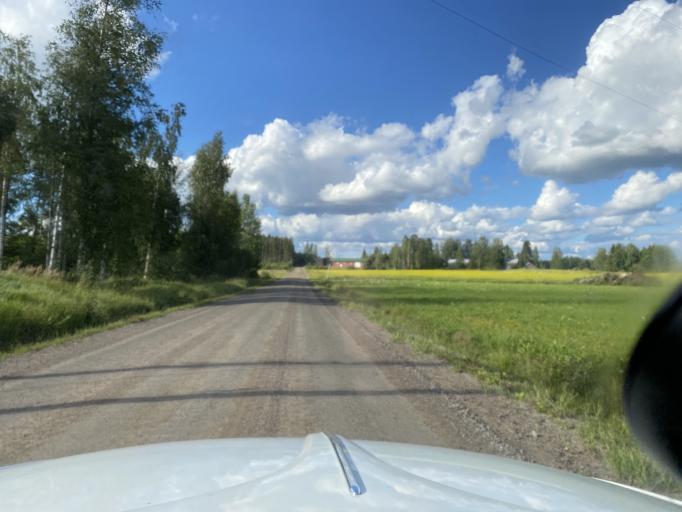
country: FI
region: Pirkanmaa
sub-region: Lounais-Pirkanmaa
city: Punkalaidun
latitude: 61.1121
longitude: 23.2745
